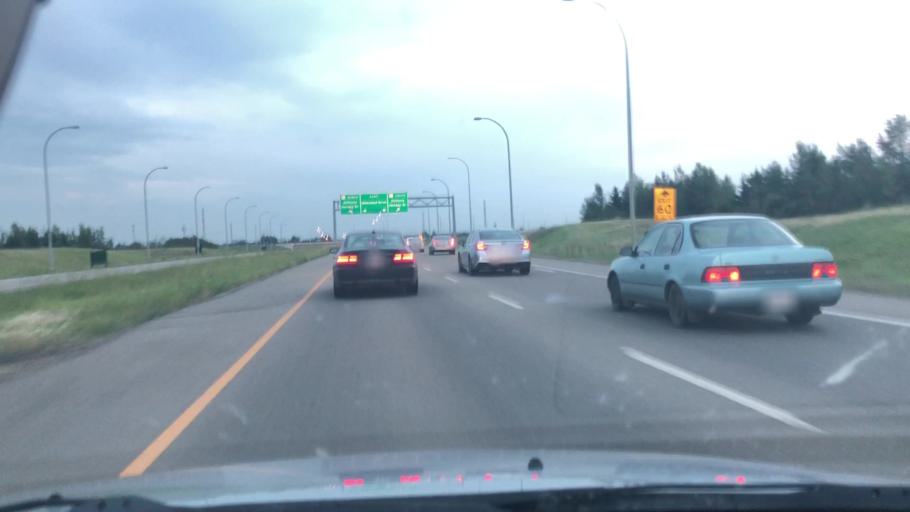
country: CA
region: Alberta
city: St. Albert
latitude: 53.5122
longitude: -113.6699
